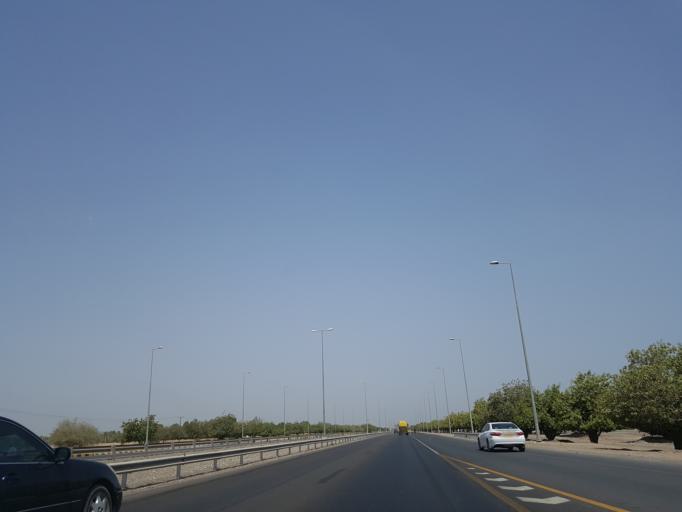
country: OM
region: Al Batinah
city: Saham
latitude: 24.1151
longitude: 56.9096
